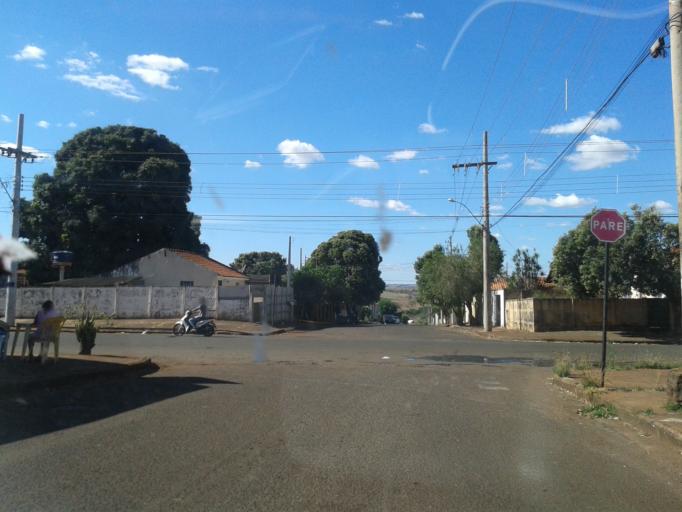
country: BR
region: Minas Gerais
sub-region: Ituiutaba
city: Ituiutaba
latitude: -18.9567
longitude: -49.4600
